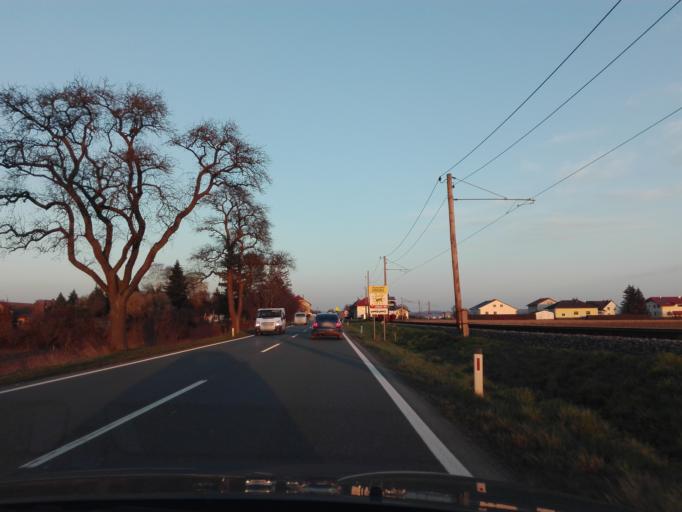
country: AT
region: Upper Austria
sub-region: Politischer Bezirk Urfahr-Umgebung
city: Goldworth
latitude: 48.2881
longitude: 14.0716
